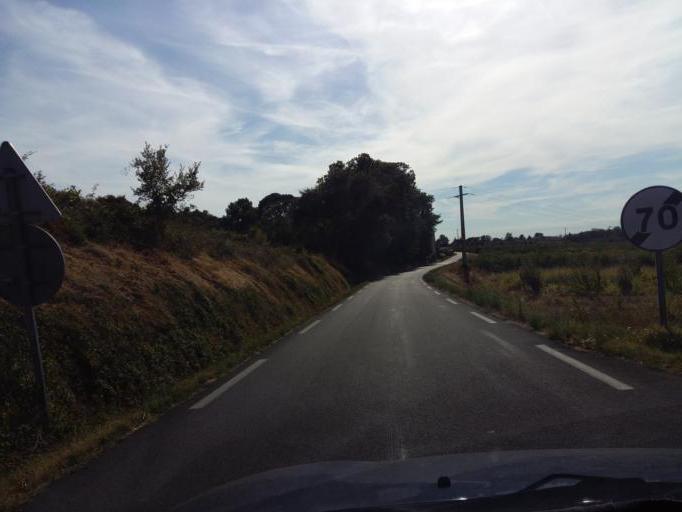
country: FR
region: Provence-Alpes-Cote d'Azur
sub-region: Departement du Vaucluse
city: Saint-Didier
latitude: 44.0092
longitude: 5.1298
